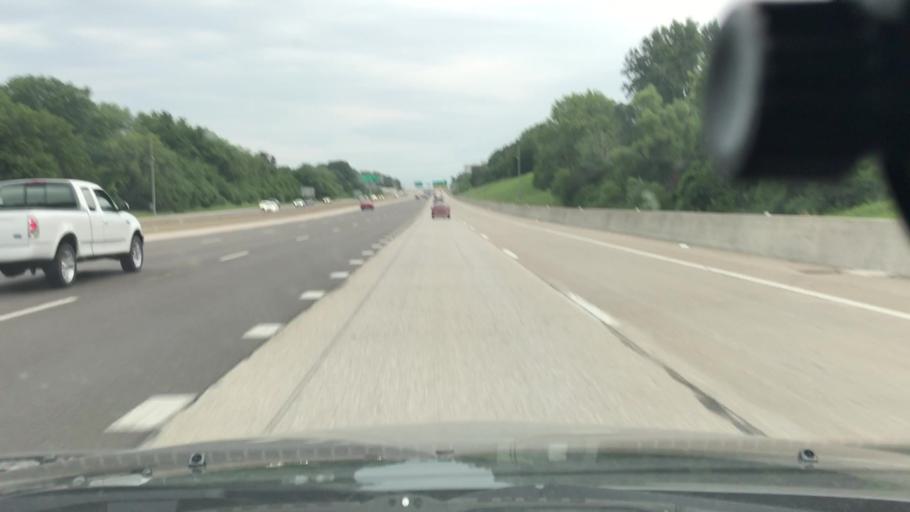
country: US
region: Missouri
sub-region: Saint Louis County
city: Creve Coeur
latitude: 38.6817
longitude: -90.4496
